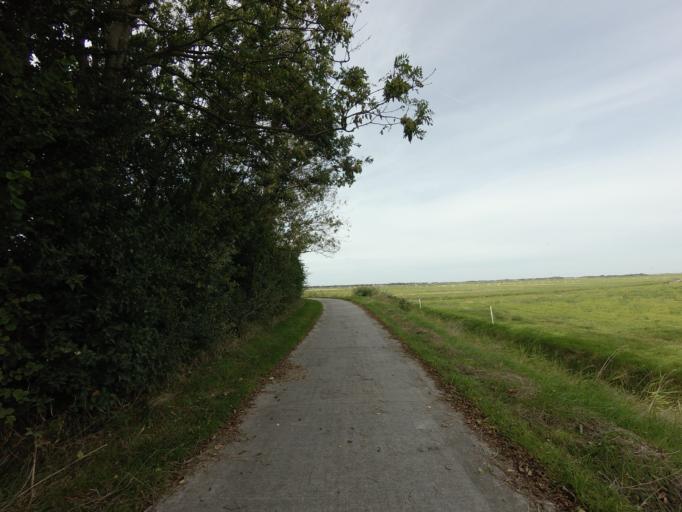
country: NL
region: North Holland
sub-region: Gemeente Texel
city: Den Burg
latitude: 53.0741
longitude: 4.8071
